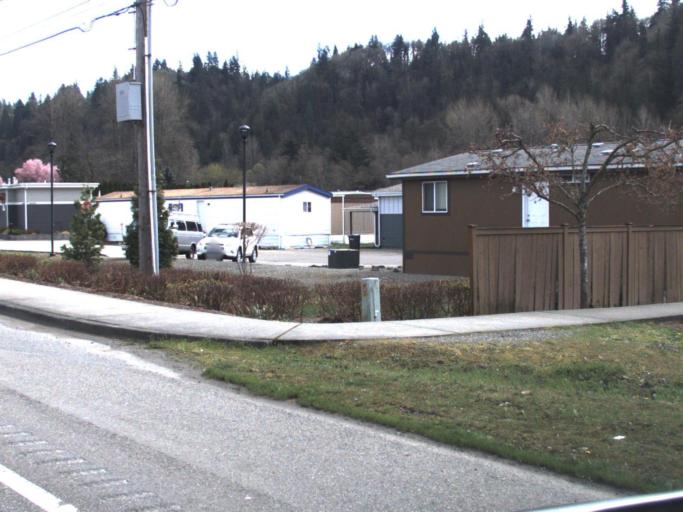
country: US
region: Washington
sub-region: King County
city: Fairwood
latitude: 47.4662
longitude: -122.1432
